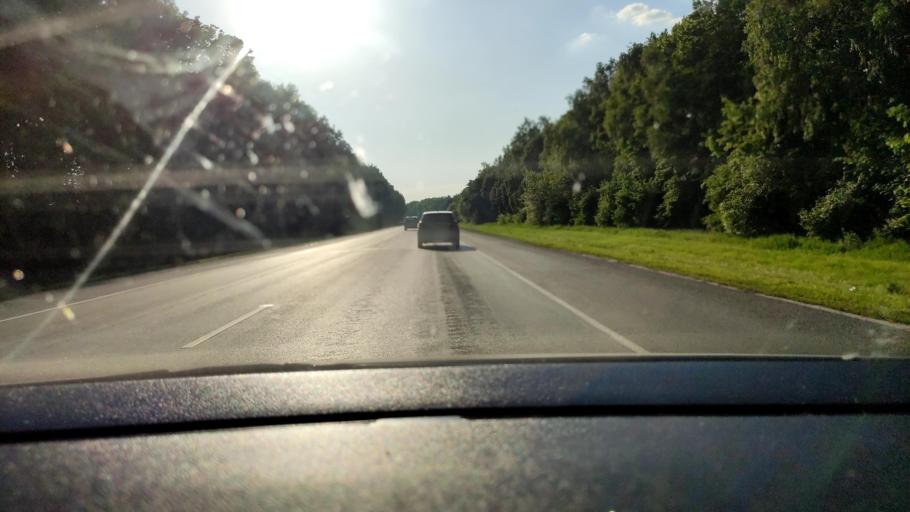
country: RU
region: Voronezj
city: Kashirskoye
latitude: 51.4894
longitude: 39.6362
